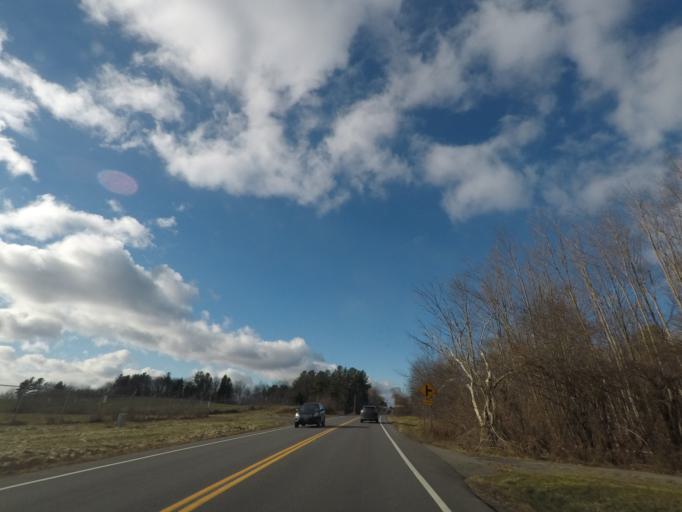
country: US
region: New York
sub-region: Schenectady County
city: East Glenville
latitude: 42.8676
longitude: -73.9212
